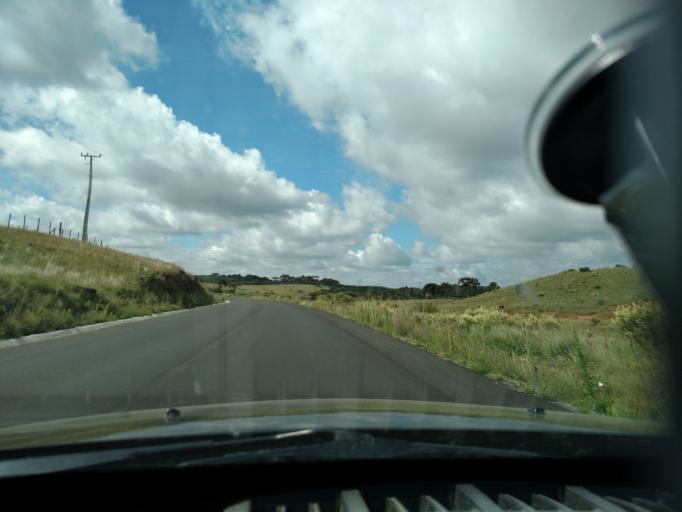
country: BR
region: Santa Catarina
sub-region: Lages
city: Lages
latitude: -28.0160
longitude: -50.0846
